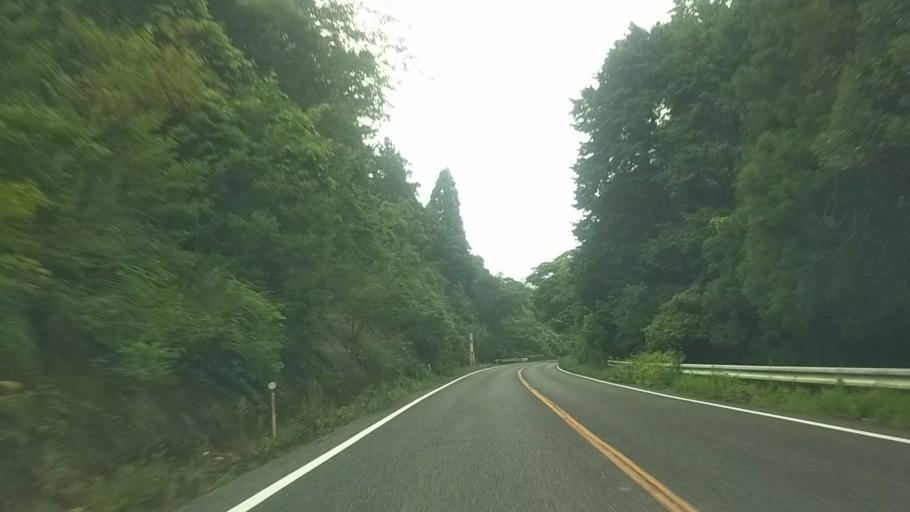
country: JP
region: Chiba
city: Kawaguchi
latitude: 35.2171
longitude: 140.0412
